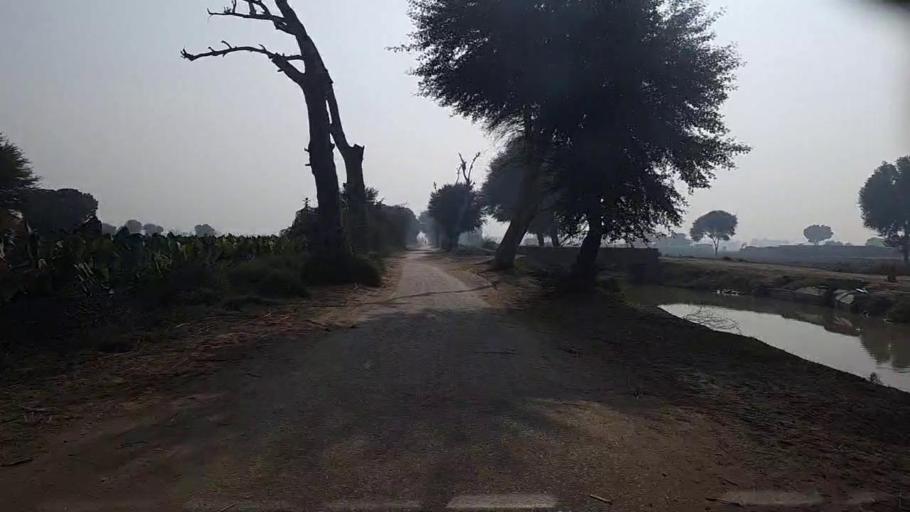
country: PK
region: Sindh
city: Setharja Old
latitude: 27.1125
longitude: 68.5091
